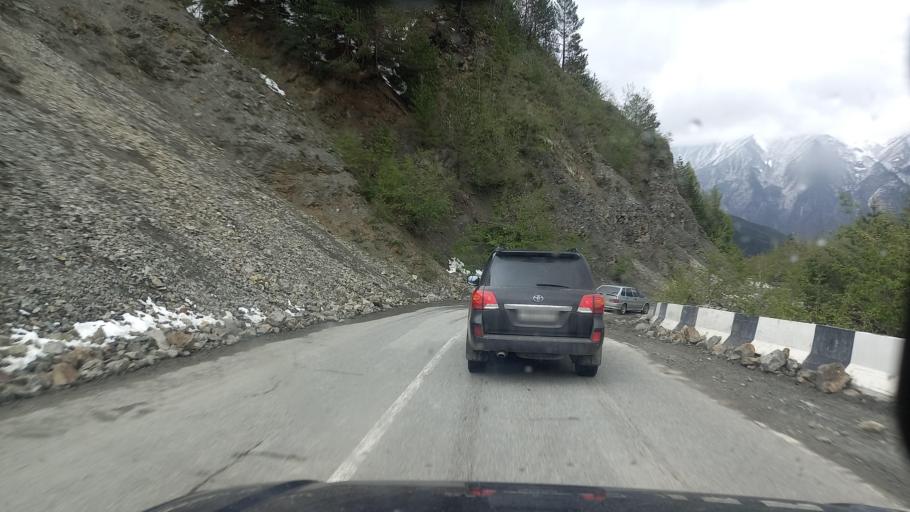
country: RU
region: North Ossetia
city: Mizur
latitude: 42.8026
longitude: 43.9523
